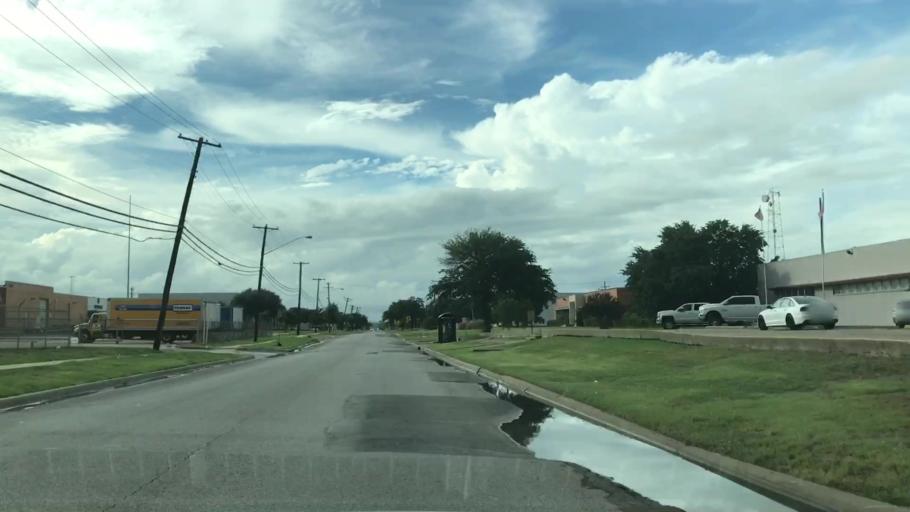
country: US
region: Texas
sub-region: Dallas County
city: Irving
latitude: 32.8167
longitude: -96.8750
